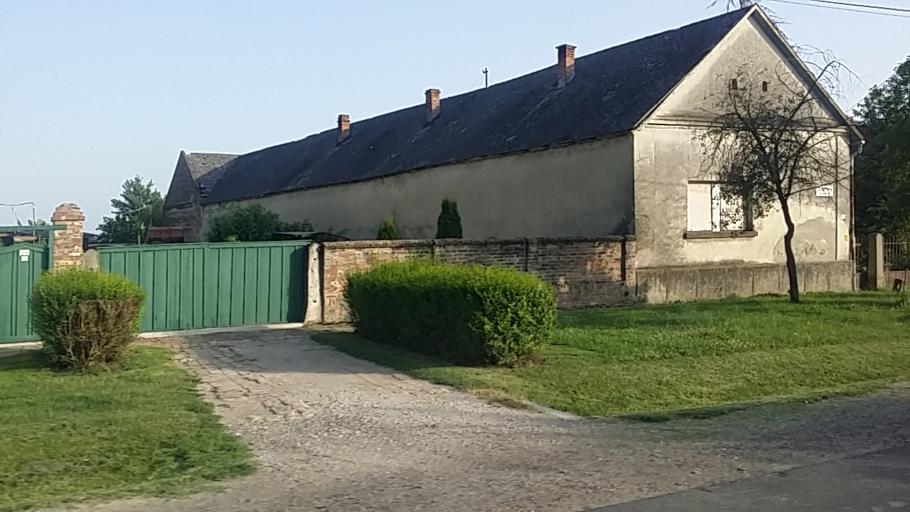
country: HU
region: Baranya
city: Villany
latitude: 45.8756
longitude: 18.4730
